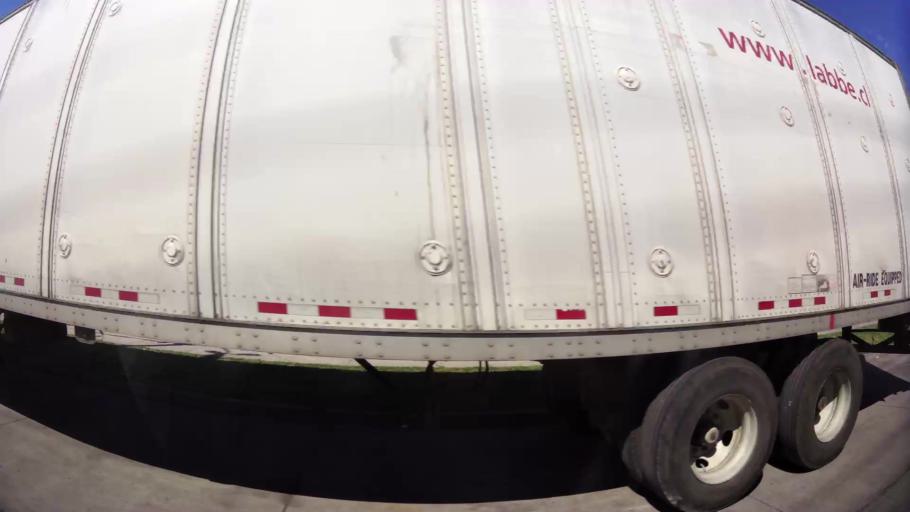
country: CL
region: Santiago Metropolitan
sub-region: Provincia de Santiago
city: Lo Prado
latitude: -33.5012
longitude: -70.7336
